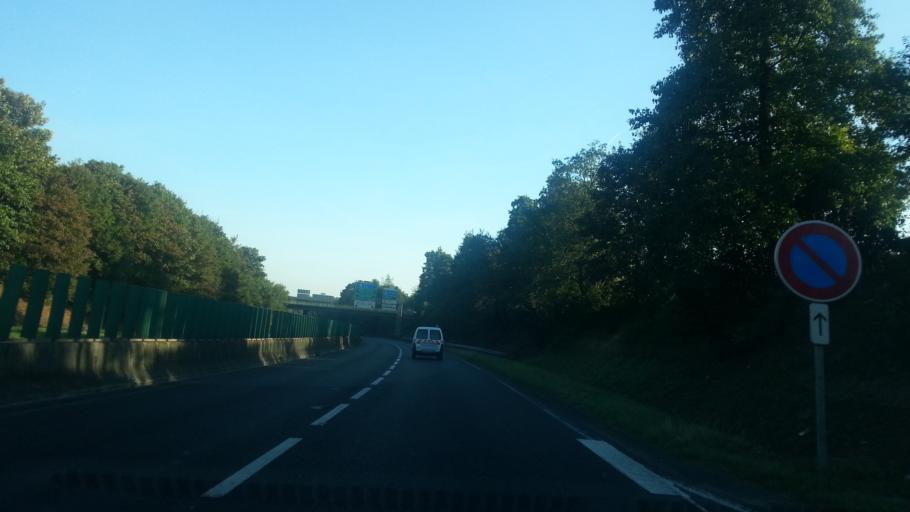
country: FR
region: Picardie
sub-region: Departement de l'Oise
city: Creil
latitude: 49.2533
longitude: 2.4911
